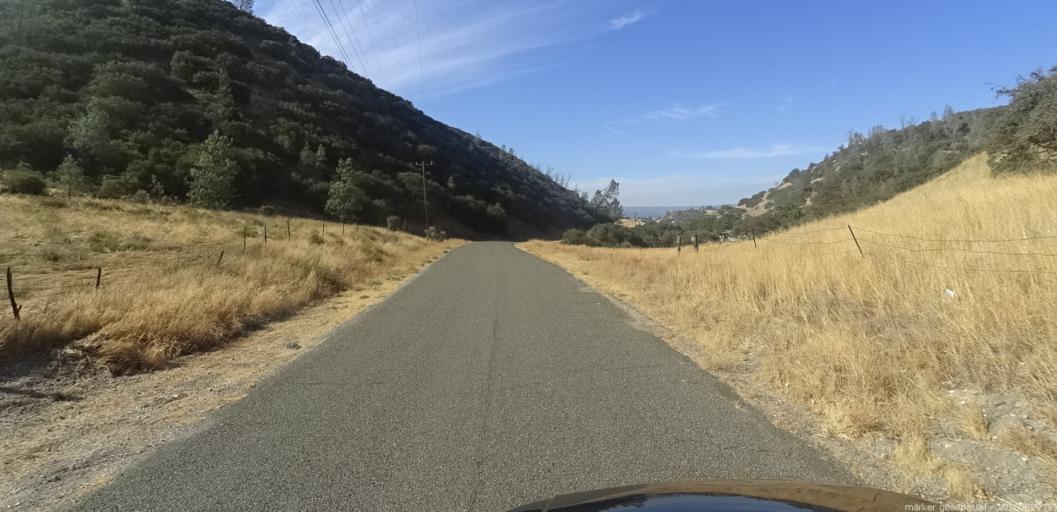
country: US
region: California
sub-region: Monterey County
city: King City
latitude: 35.9952
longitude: -121.0719
